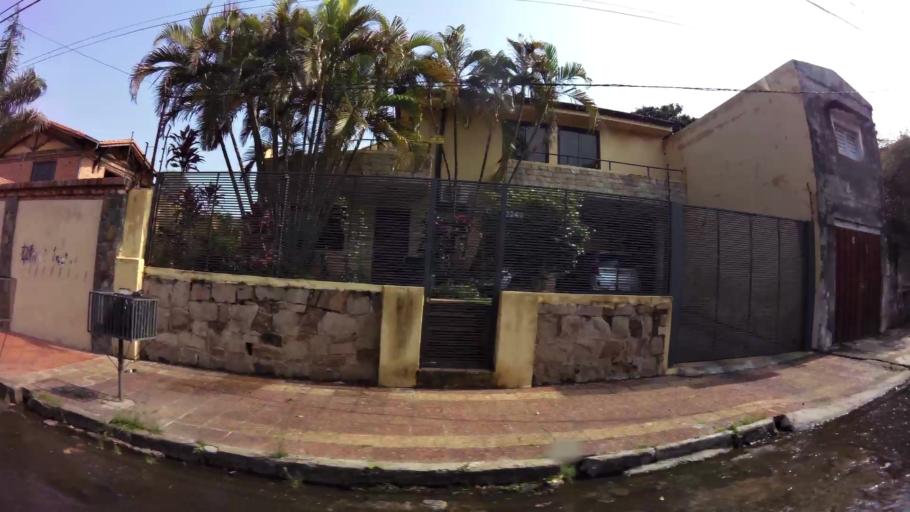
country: PY
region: Presidente Hayes
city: Nanawa
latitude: -25.2934
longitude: -57.6655
